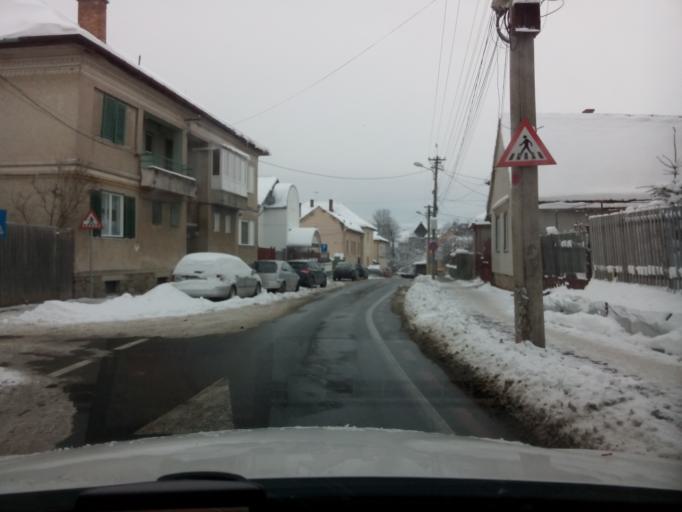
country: RO
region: Sibiu
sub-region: Municipiul Sibiu
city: Sibiu
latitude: 45.7906
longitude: 24.1415
